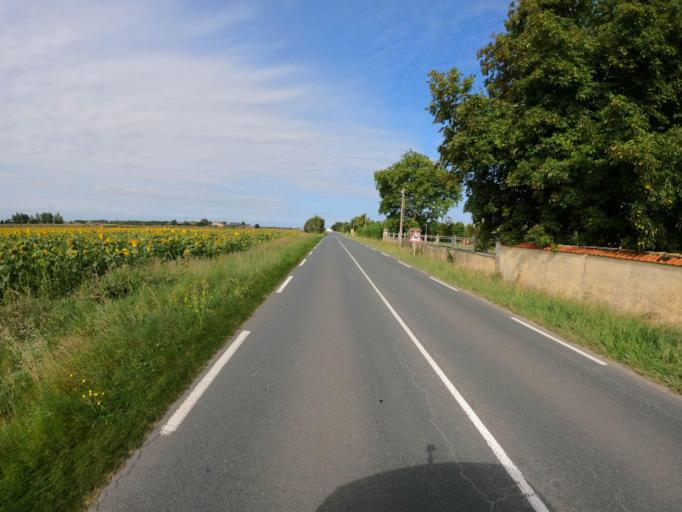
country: FR
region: Pays de la Loire
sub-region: Departement de la Vendee
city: Triaize
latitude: 46.3680
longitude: -1.2272
